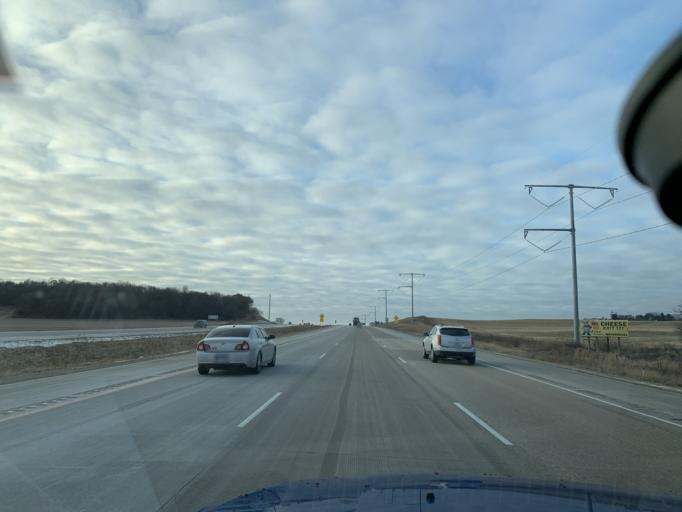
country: US
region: Wisconsin
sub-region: Dane County
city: Cottage Grove
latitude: 43.0065
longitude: -89.2143
